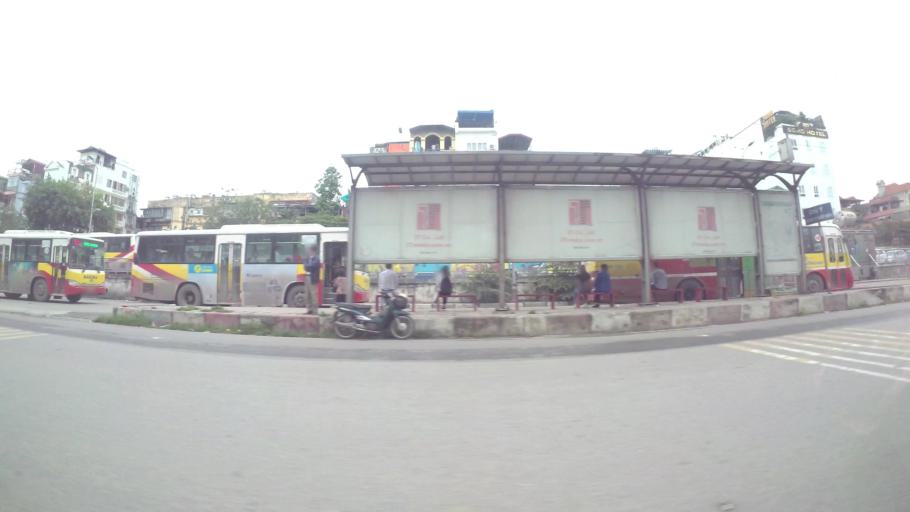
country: VN
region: Ha Noi
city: Hoan Kiem
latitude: 21.0222
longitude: 105.8611
